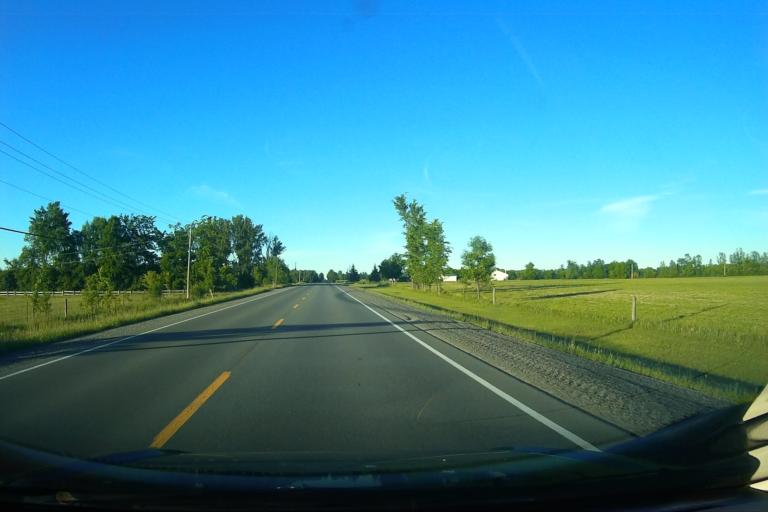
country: CA
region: Ontario
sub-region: Lanark County
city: Smiths Falls
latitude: 44.9807
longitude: -75.7304
